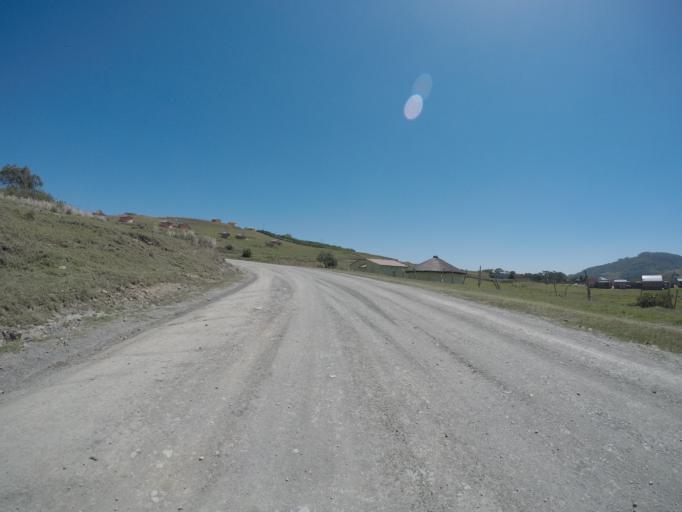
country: ZA
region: Eastern Cape
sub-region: OR Tambo District Municipality
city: Libode
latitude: -32.0198
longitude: 29.0818
